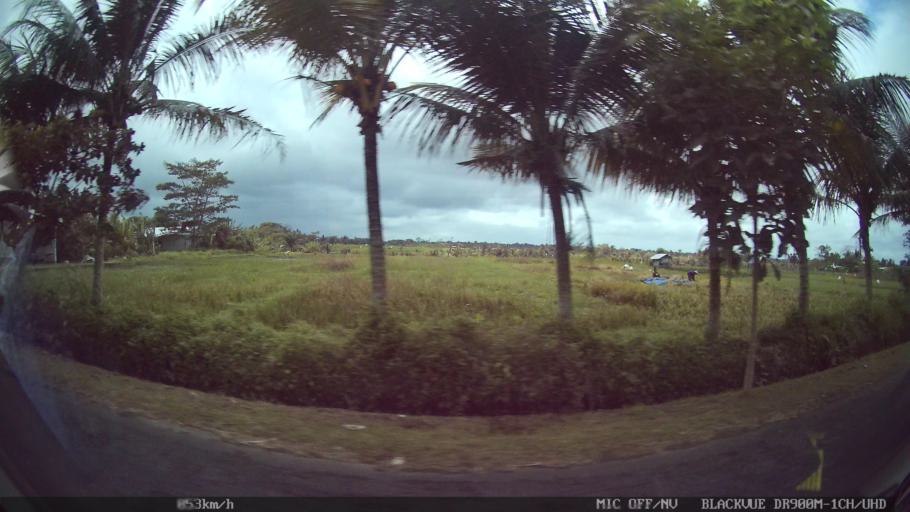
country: ID
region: Bali
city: Banjar Serangan
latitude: -8.5274
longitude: 115.1807
